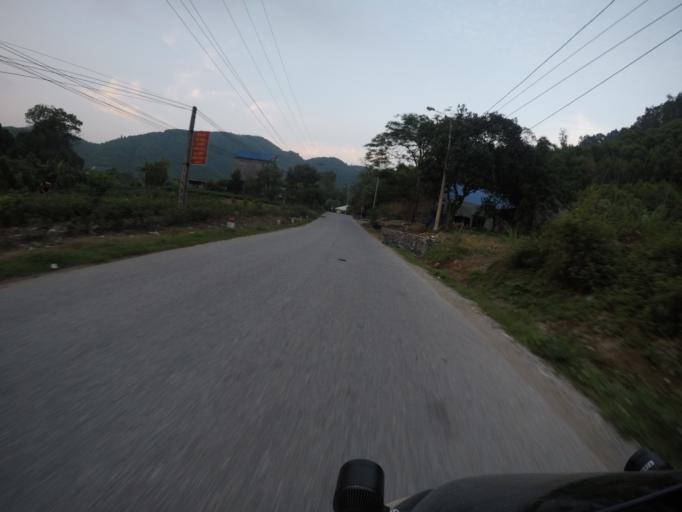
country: VN
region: Thai Nguyen
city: Chua Hang
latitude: 21.5870
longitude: 105.7097
